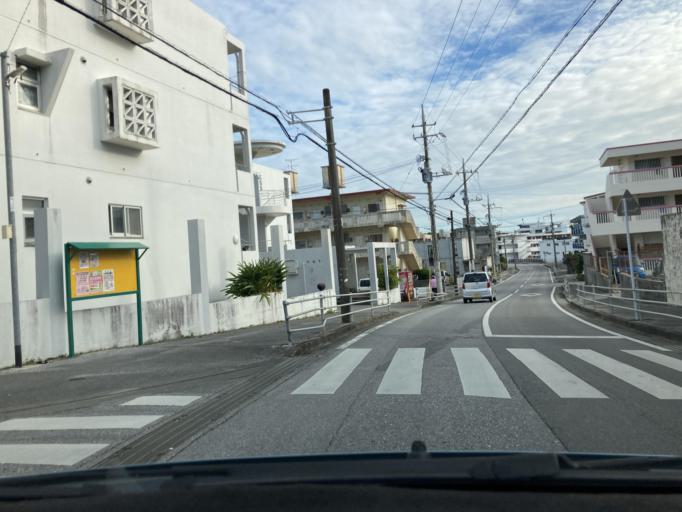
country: JP
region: Okinawa
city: Tomigusuku
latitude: 26.2004
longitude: 127.7317
